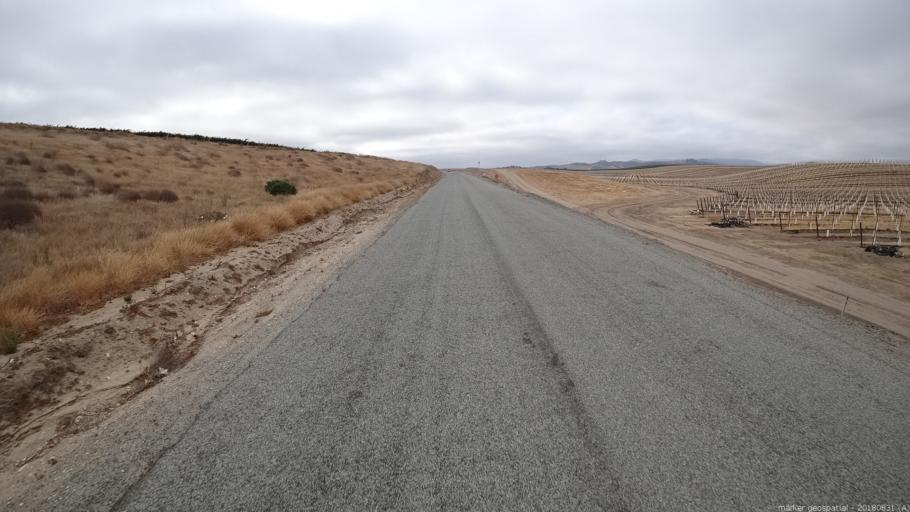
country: US
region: California
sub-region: Monterey County
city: King City
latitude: 36.1617
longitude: -121.1121
